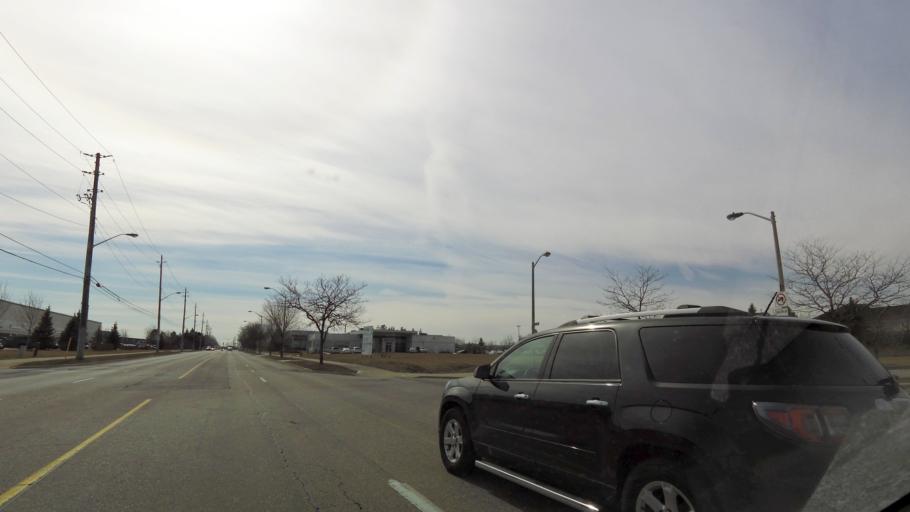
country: CA
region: Ontario
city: Burlington
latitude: 43.3905
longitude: -79.7777
